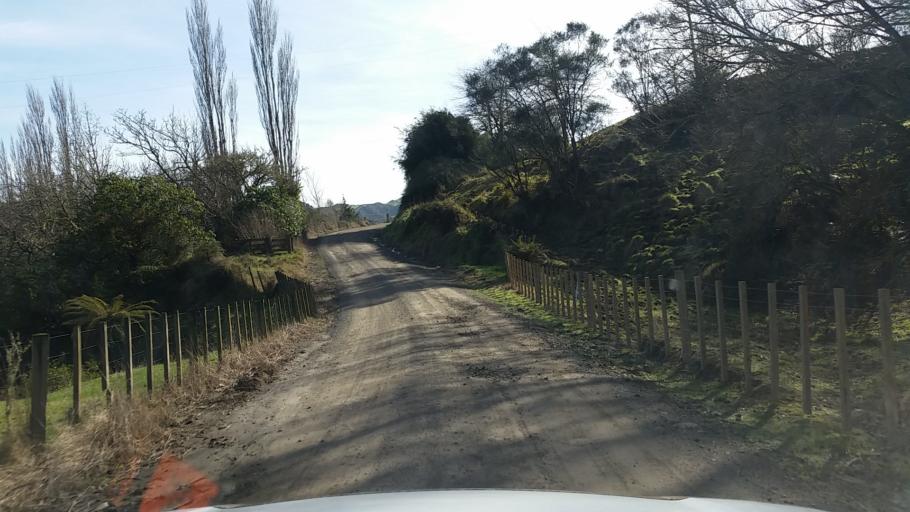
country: NZ
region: Taranaki
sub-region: South Taranaki District
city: Eltham
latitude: -39.3569
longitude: 174.5120
